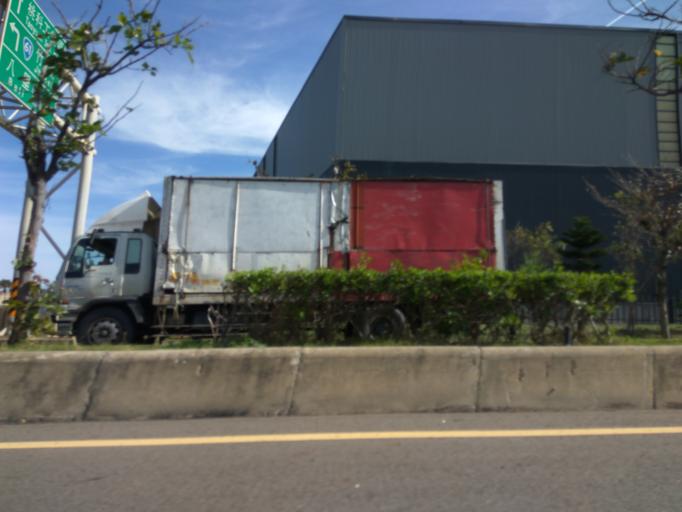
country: TW
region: Taiwan
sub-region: Hsinchu
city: Zhubei
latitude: 25.0373
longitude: 121.0665
